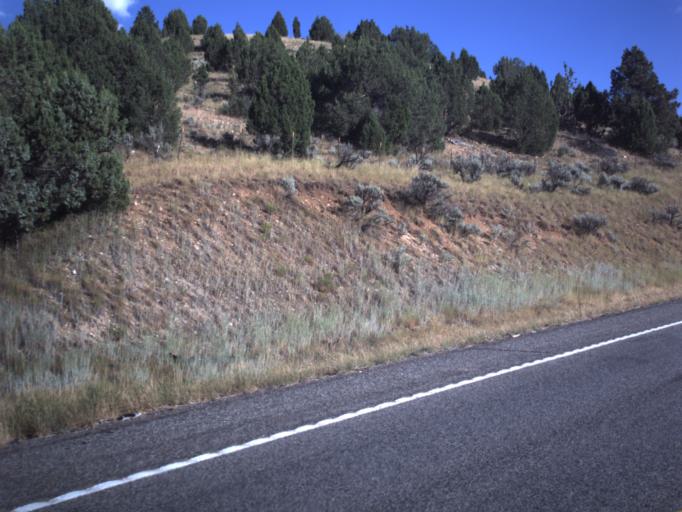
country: US
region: Utah
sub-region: Utah County
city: Woodland Hills
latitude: 39.9014
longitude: -111.5492
